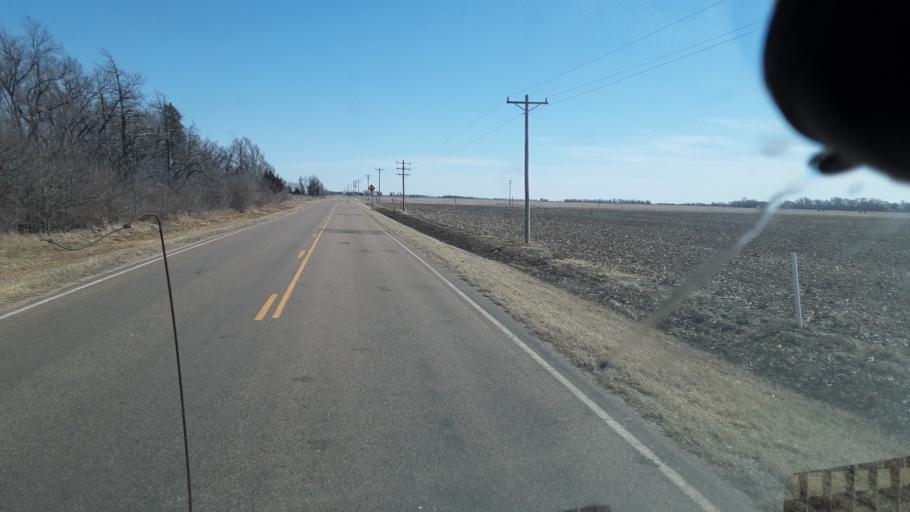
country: US
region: Kansas
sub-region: Rice County
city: Sterling
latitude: 38.2462
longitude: -98.2099
